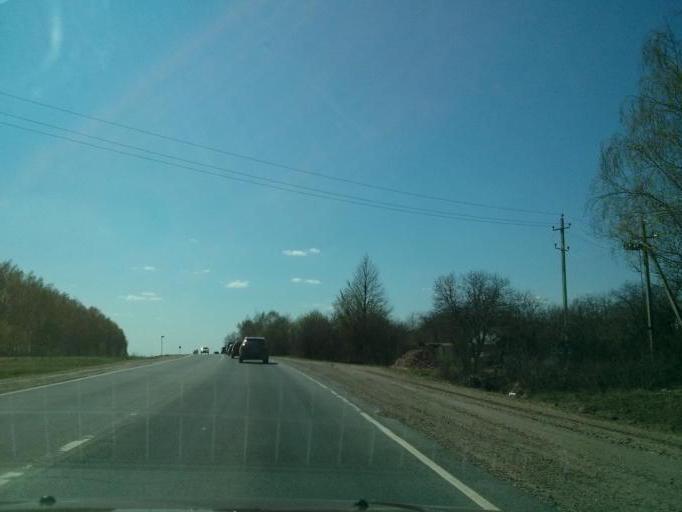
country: RU
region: Nizjnij Novgorod
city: Burevestnik
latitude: 56.1937
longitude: 43.8376
